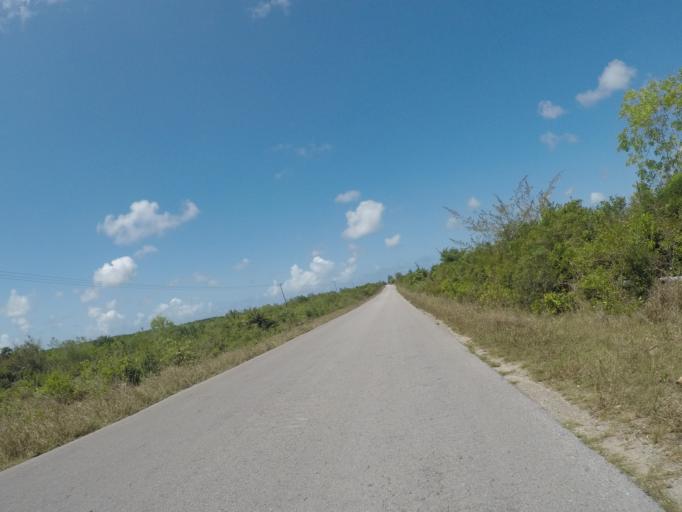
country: TZ
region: Zanzibar Central/South
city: Nganane
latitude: -6.2851
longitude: 39.4563
